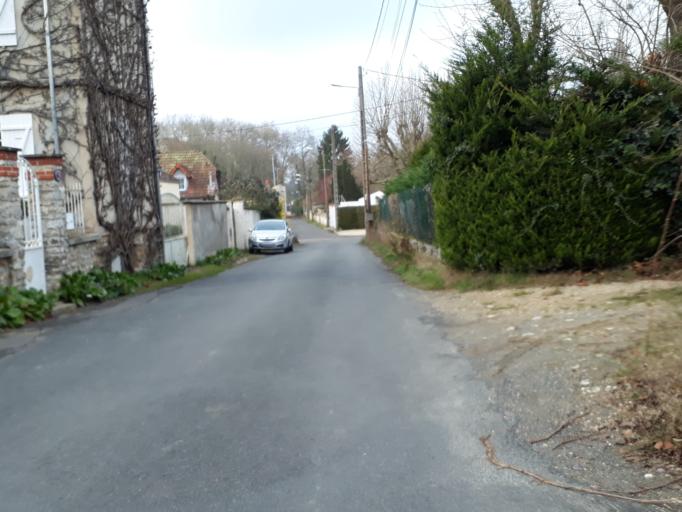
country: FR
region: Ile-de-France
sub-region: Departement de Seine-et-Marne
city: Chartrettes
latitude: 48.4777
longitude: 2.6812
